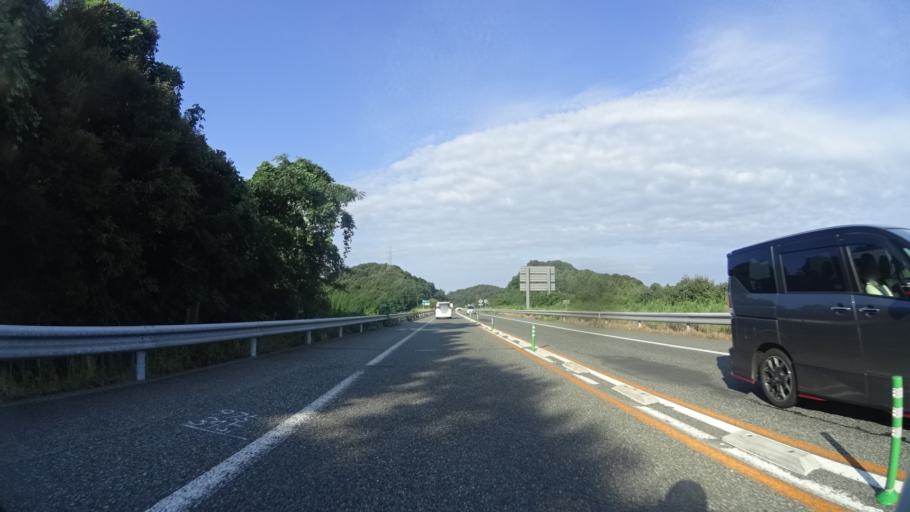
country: JP
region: Shimane
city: Hiratacho
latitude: 35.3969
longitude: 132.9176
